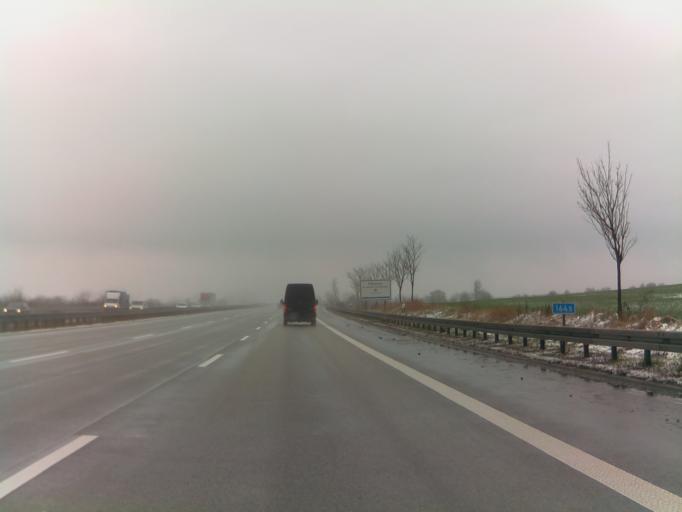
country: DE
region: Saxony-Anhalt
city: Osterfeld
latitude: 51.0516
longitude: 11.9445
